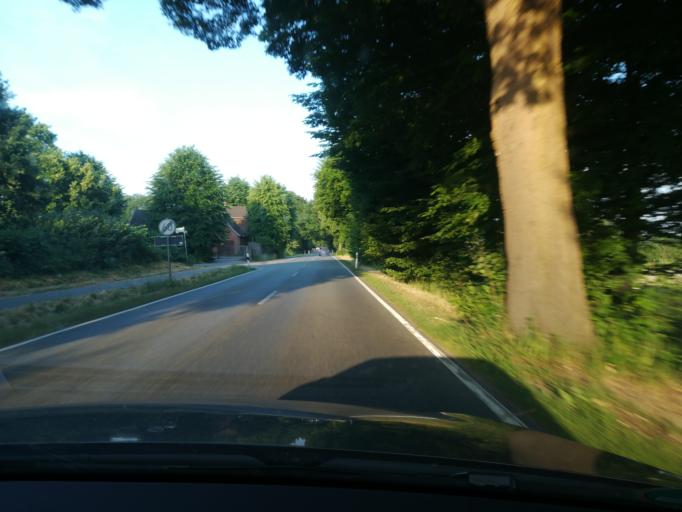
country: DE
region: Schleswig-Holstein
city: Grossensee
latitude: 53.6137
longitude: 10.3679
